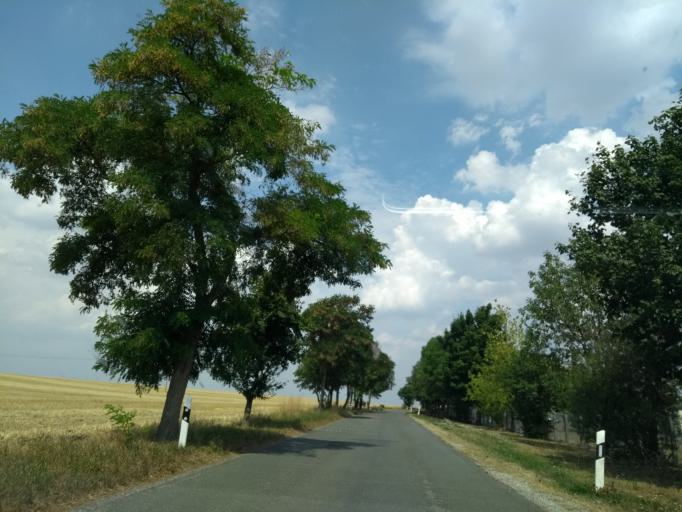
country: DE
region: Thuringia
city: Walpernhain
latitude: 50.9968
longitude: 11.9488
